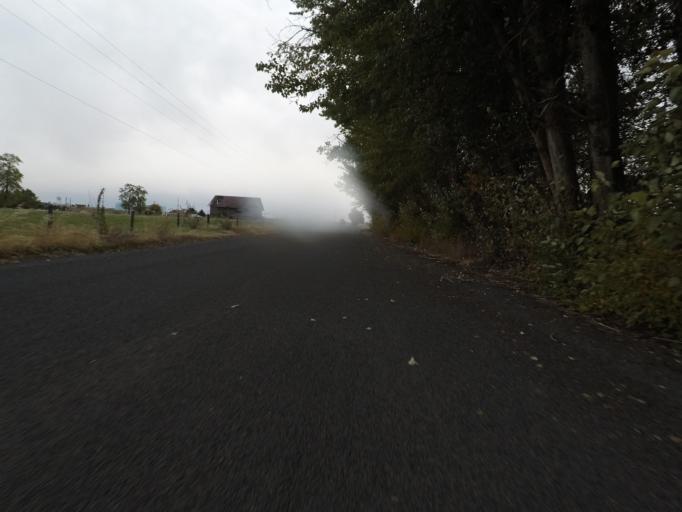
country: US
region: Washington
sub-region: Walla Walla County
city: Walla Walla East
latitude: 46.0833
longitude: -118.2525
